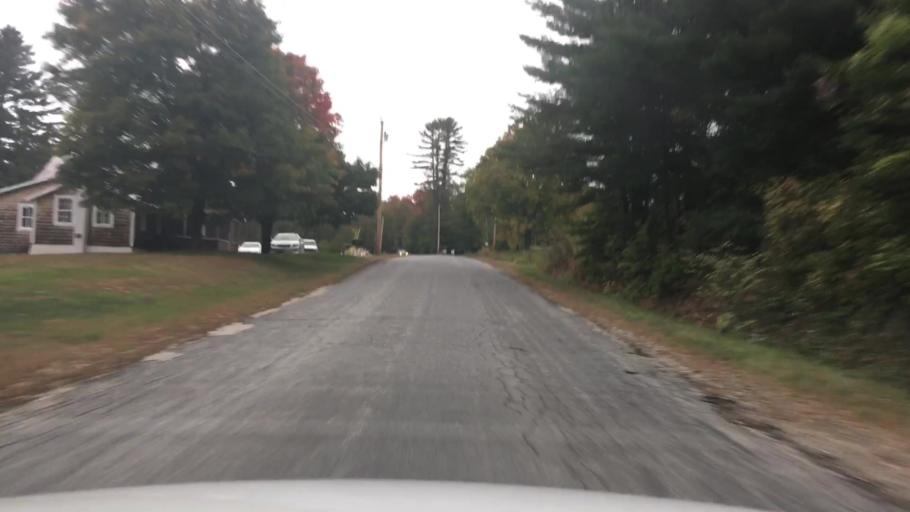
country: US
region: Maine
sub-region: Oxford County
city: Bethel
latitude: 44.4693
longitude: -70.7843
